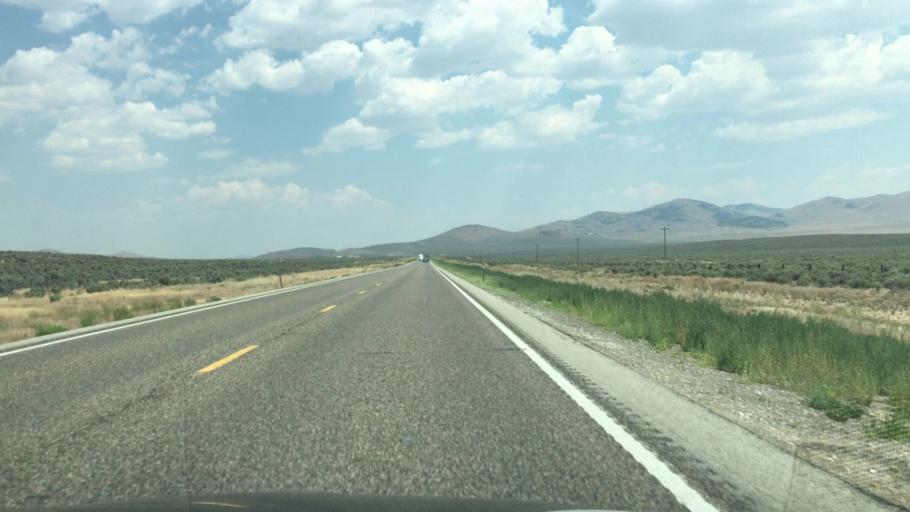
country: US
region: Nevada
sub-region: Elko County
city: Wells
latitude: 41.1494
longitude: -114.9044
